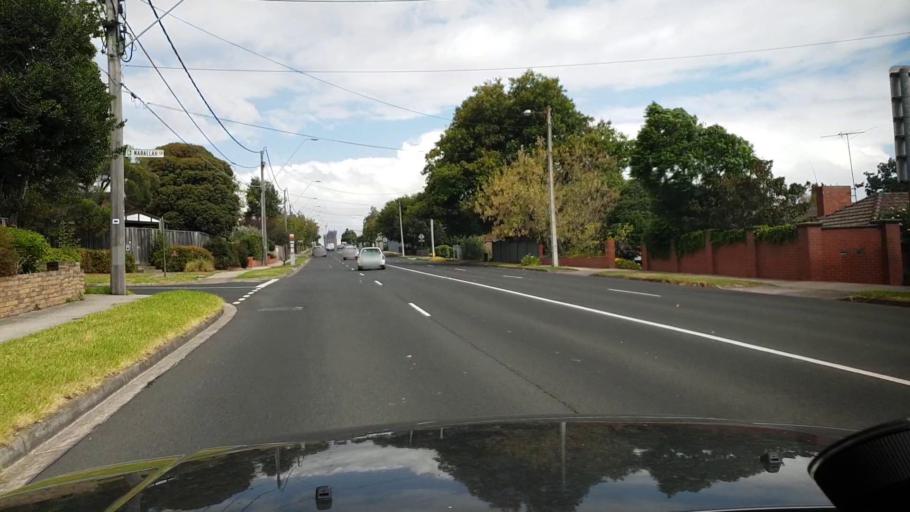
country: AU
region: Victoria
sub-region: Whitehorse
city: Box Hill North
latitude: -37.7997
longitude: 145.1273
